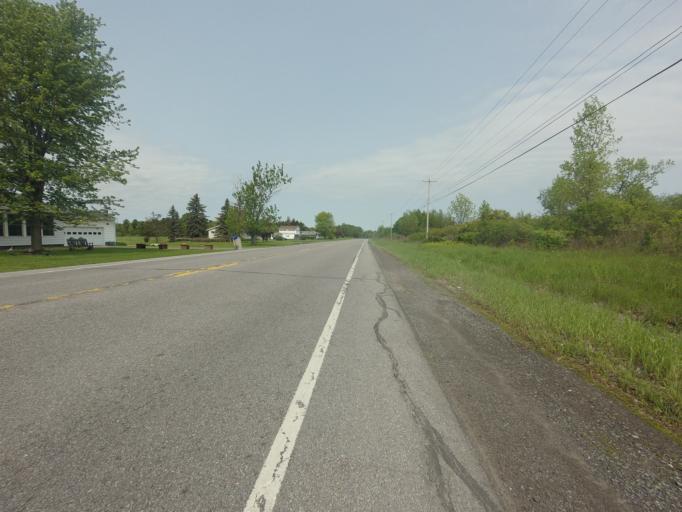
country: US
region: New York
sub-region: Jefferson County
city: Brownville
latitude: 44.0046
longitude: -76.0072
